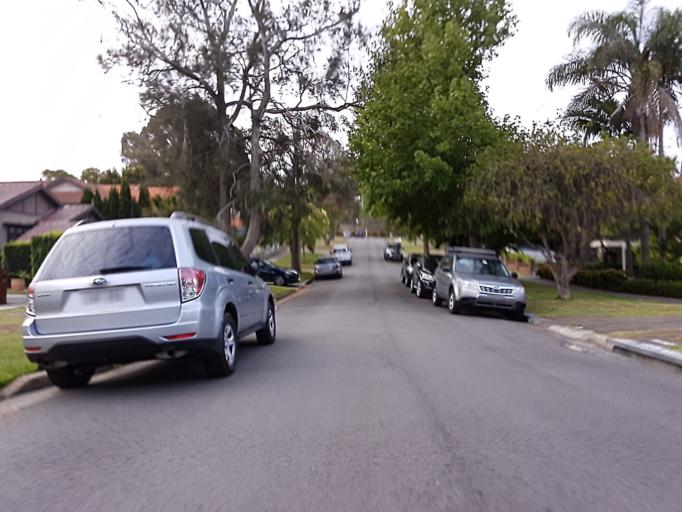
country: AU
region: New South Wales
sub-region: Willoughby
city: Castle Cove
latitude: -33.7992
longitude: 151.2076
